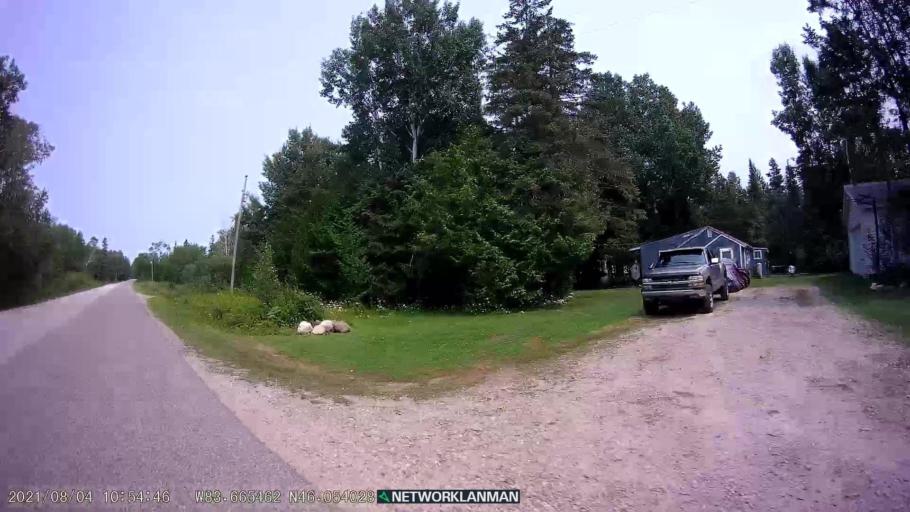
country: CA
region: Ontario
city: Thessalon
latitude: 46.0550
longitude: -83.6655
